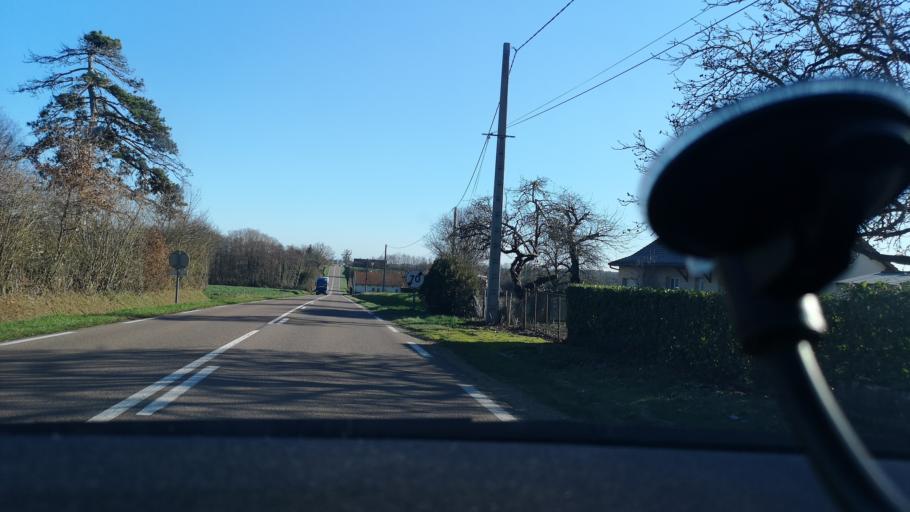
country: FR
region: Bourgogne
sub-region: Departement de Saone-et-Loire
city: Saint-Germain-du-Plain
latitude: 46.7526
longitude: 5.0267
